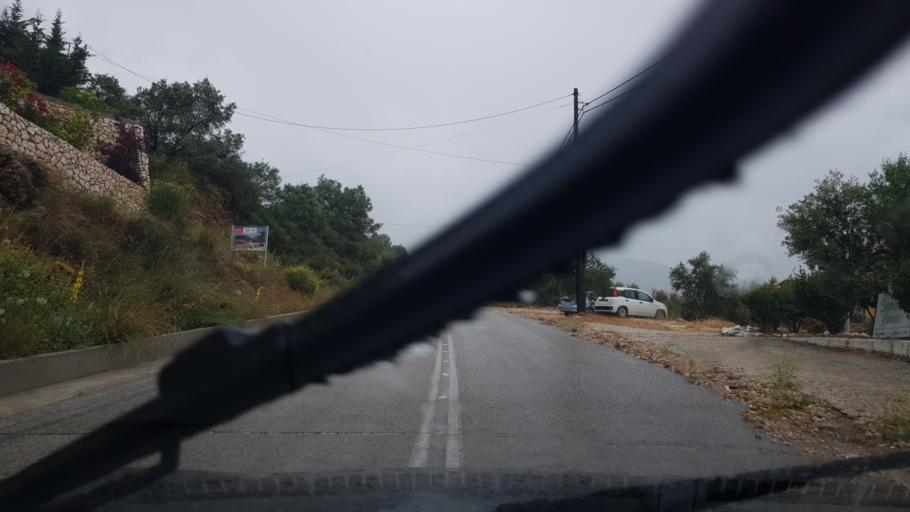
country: GR
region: Ionian Islands
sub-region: Lefkada
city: Nidri
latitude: 38.6414
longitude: 20.5968
